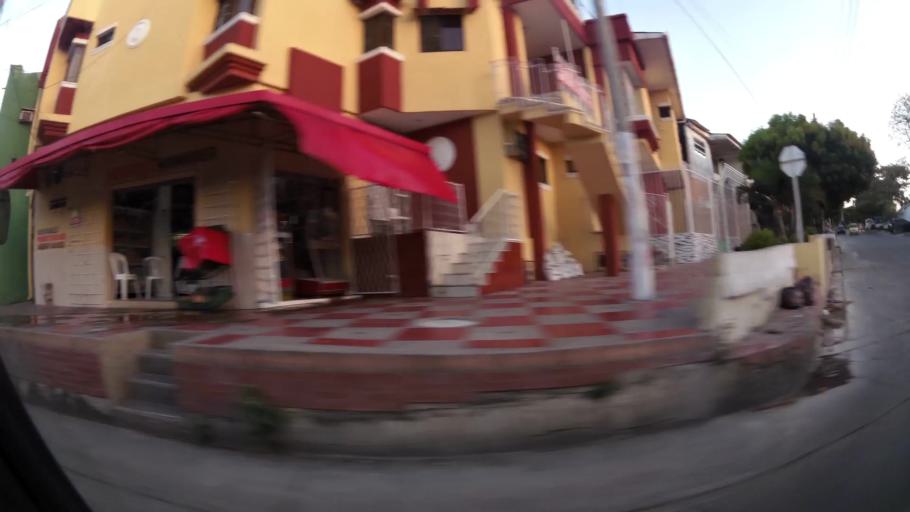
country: CO
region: Atlantico
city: Barranquilla
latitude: 10.9825
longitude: -74.8024
